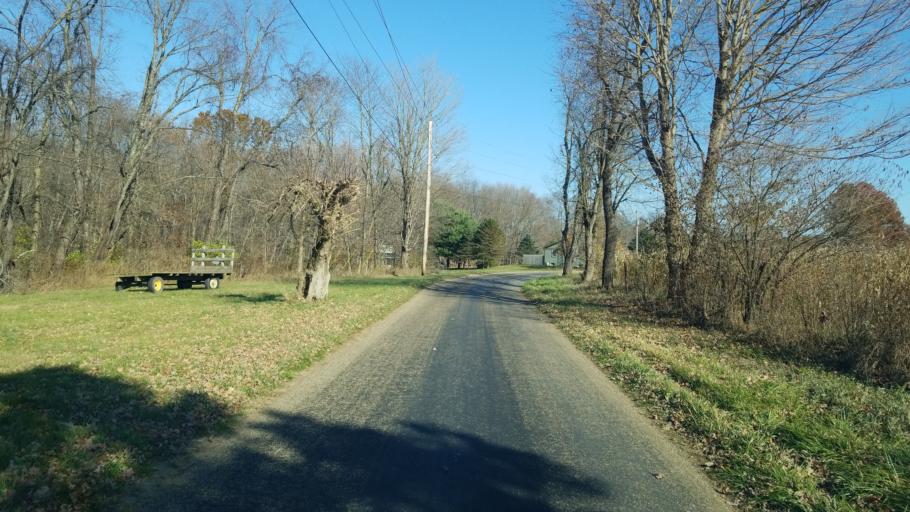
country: US
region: Ohio
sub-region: Licking County
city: Newark
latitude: 40.1229
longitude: -82.3573
